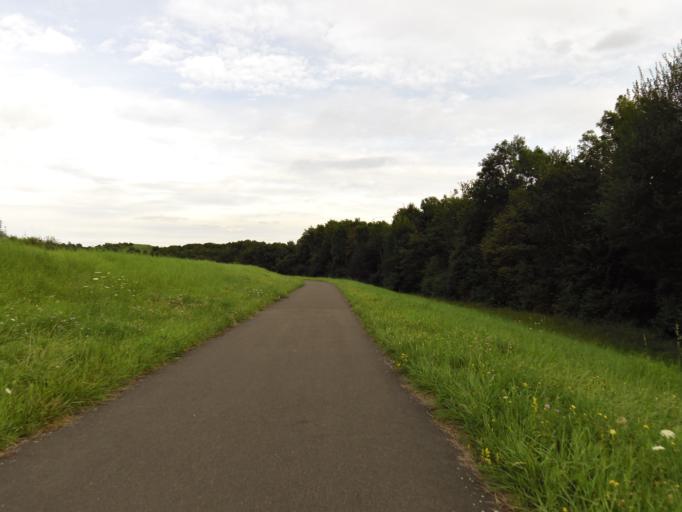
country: DE
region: Rheinland-Pfalz
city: Bobenheim-Roxheim
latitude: 49.6065
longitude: 8.3863
